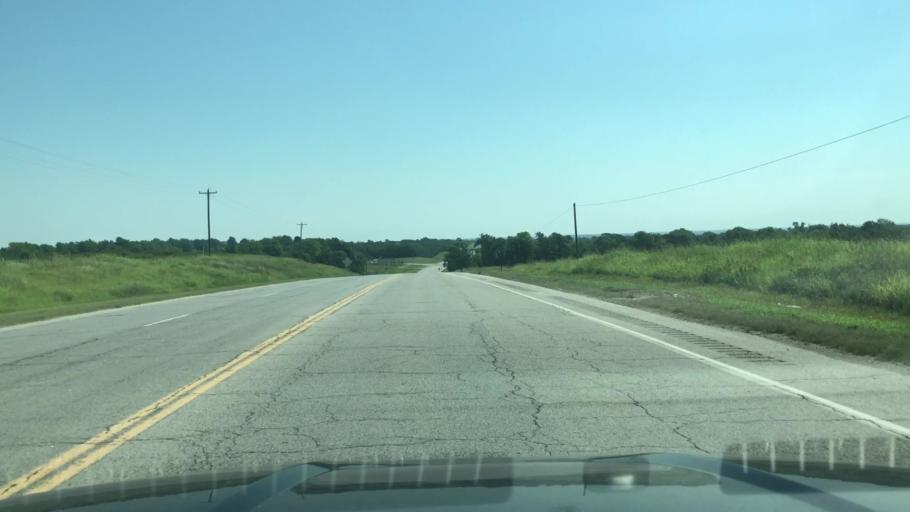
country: US
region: Oklahoma
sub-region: Creek County
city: Drumright
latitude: 35.9937
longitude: -96.5333
